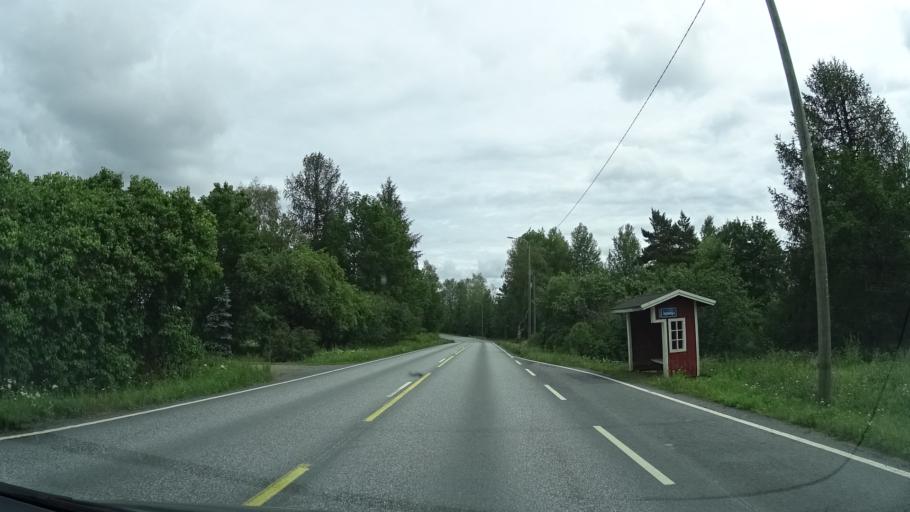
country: FI
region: Pirkanmaa
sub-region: Etelae-Pirkanmaa
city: Urjala
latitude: 61.0828
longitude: 23.4288
